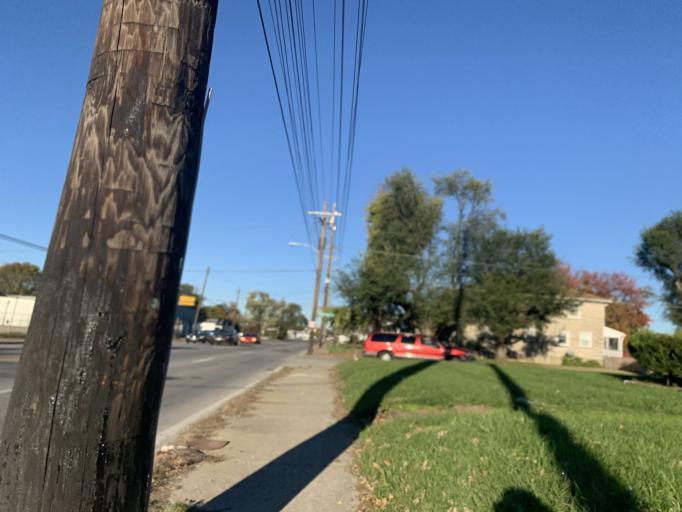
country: US
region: Kentucky
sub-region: Jefferson County
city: Louisville
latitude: 38.2175
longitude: -85.7801
